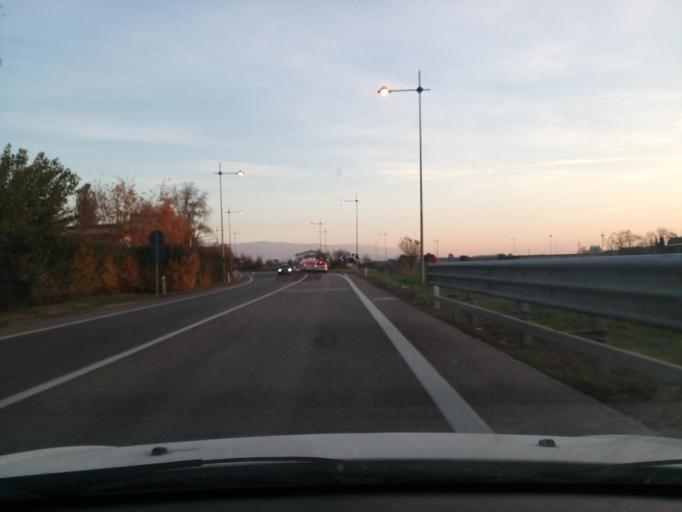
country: IT
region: Veneto
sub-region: Provincia di Vicenza
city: Thiene
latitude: 45.6859
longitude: 11.4674
